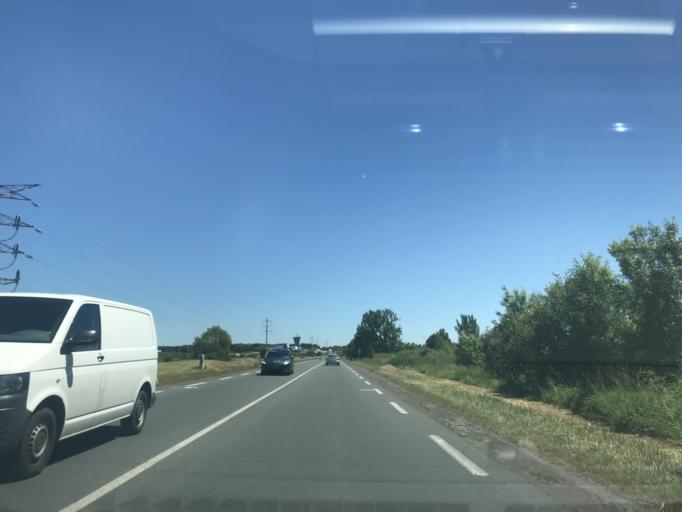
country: FR
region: Poitou-Charentes
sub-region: Departement de la Charente-Maritime
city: Royan
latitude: 45.6359
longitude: -1.0161
